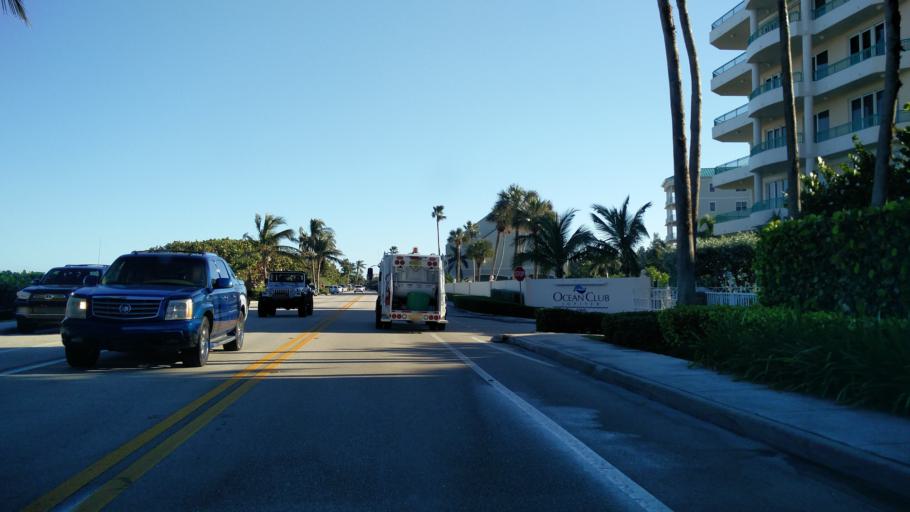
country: US
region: Florida
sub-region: Palm Beach County
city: Jupiter
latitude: 26.9150
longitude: -80.0644
